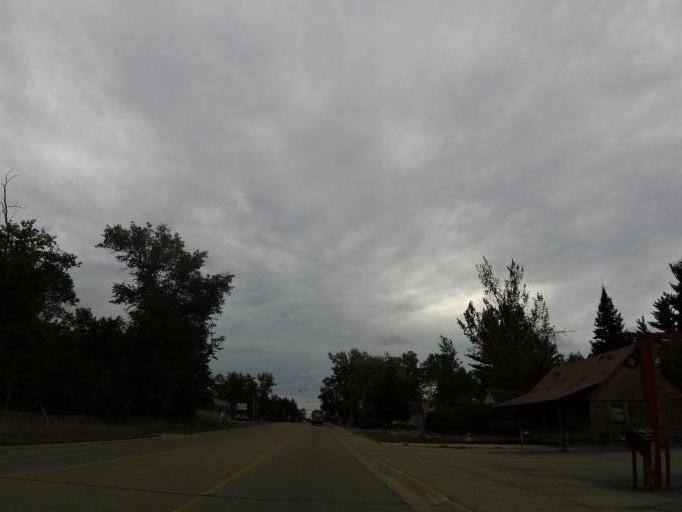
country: US
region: Michigan
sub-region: Roscommon County
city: Saint Helen
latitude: 44.3706
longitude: -84.4103
